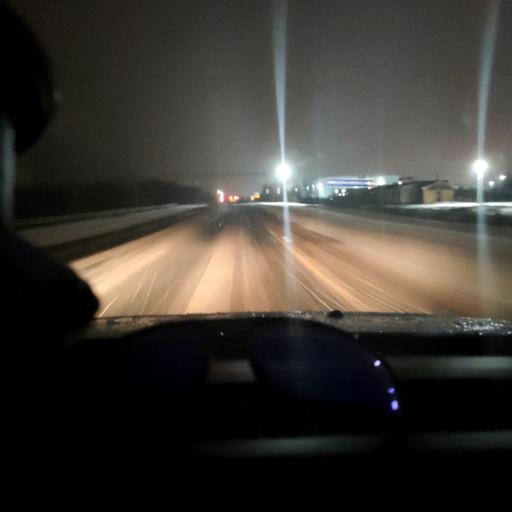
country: RU
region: Samara
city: Samara
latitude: 53.0811
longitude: 50.1202
